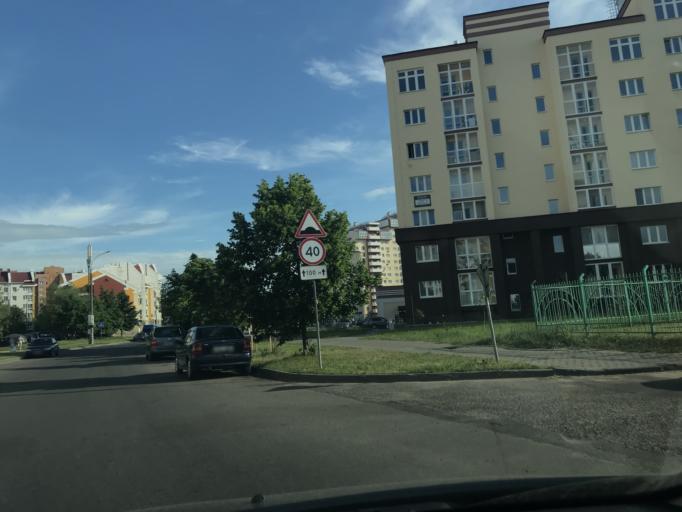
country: BY
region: Minsk
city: Borovlyany
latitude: 53.9510
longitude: 27.6833
